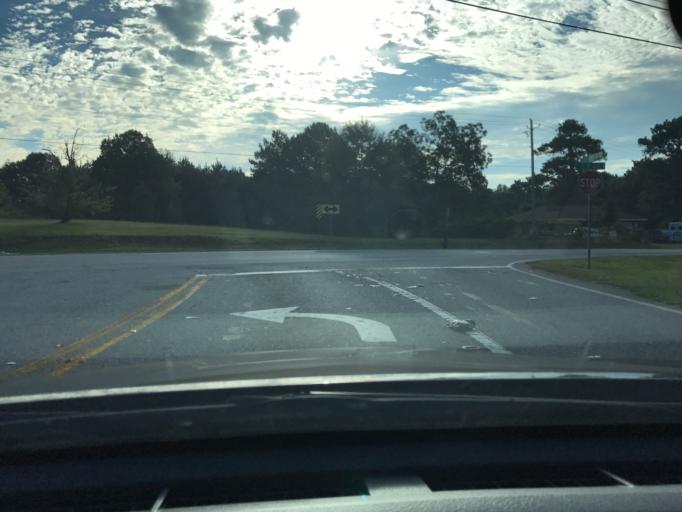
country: US
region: Georgia
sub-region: Clayton County
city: Lake City
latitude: 33.6005
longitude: -84.2990
